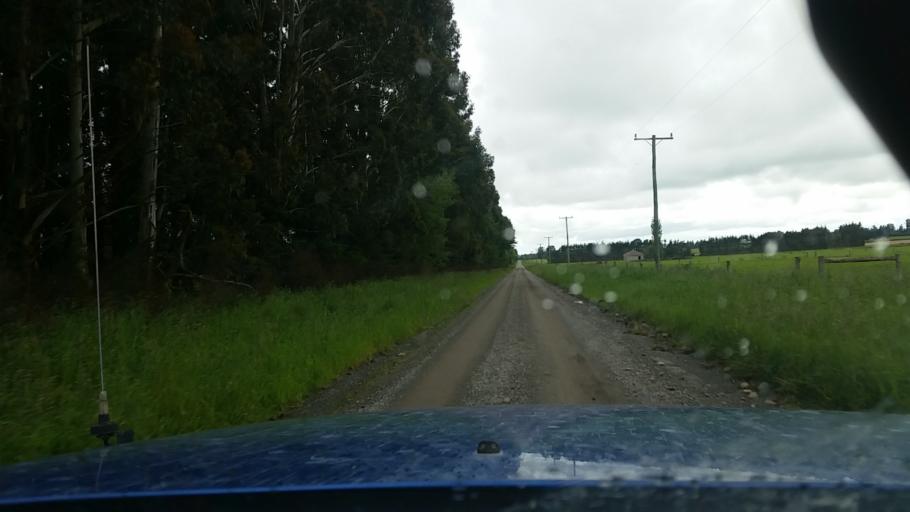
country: NZ
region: Canterbury
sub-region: Ashburton District
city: Methven
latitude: -43.6953
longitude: 171.4130
